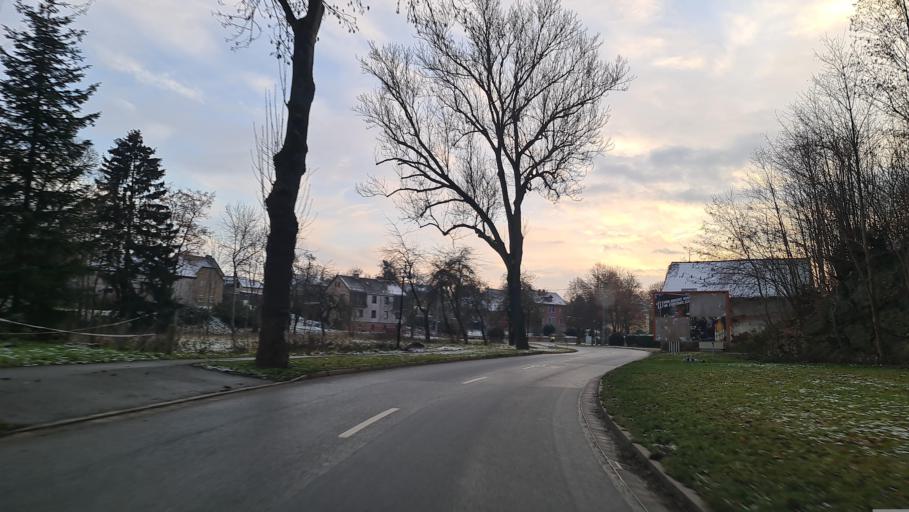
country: DE
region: Saxony
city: Limbach
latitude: 50.5873
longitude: 12.2582
